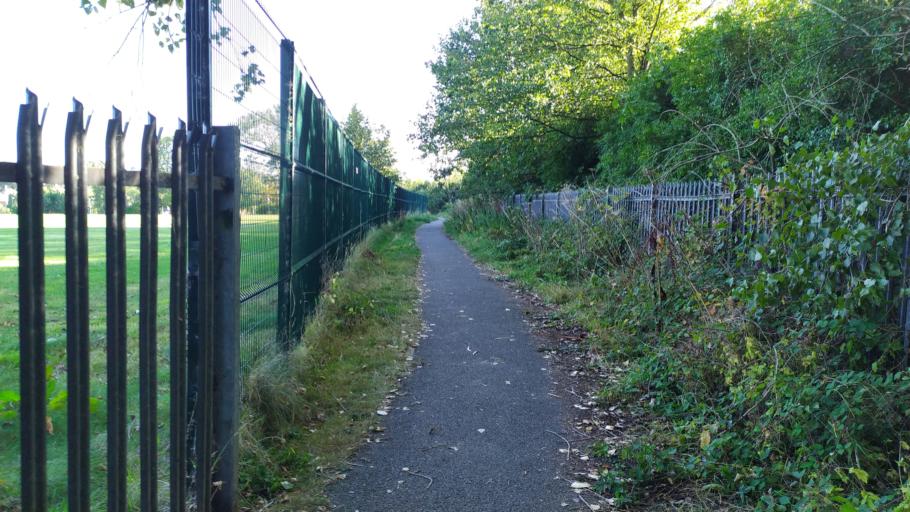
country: GB
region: England
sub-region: City and Borough of Leeds
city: Chapel Allerton
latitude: 53.8331
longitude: -1.5574
